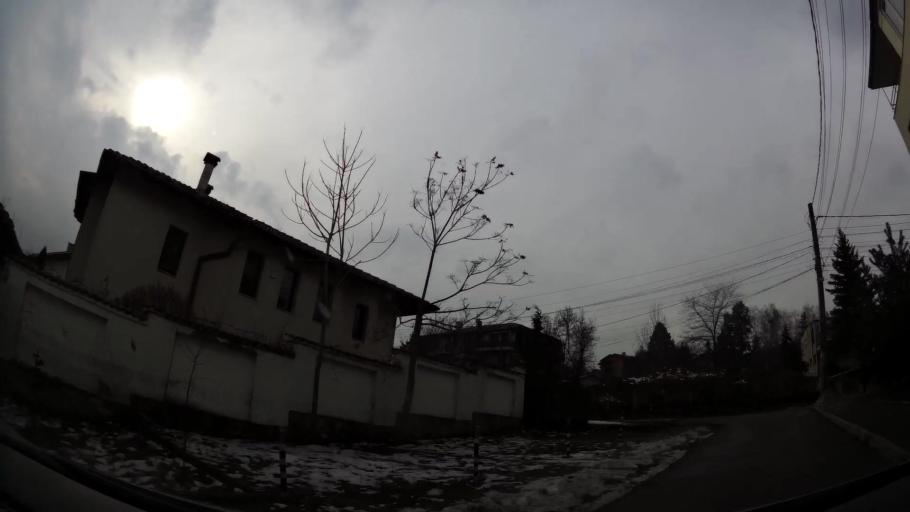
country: BG
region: Sofia-Capital
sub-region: Stolichna Obshtina
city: Sofia
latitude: 42.6657
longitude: 23.2442
